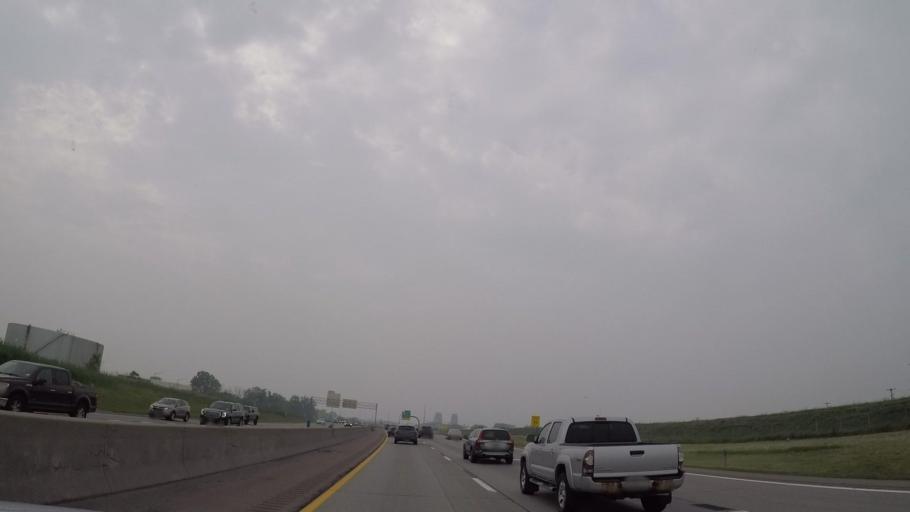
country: US
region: New York
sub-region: Erie County
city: Grandyle Village
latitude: 42.9917
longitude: -78.9236
